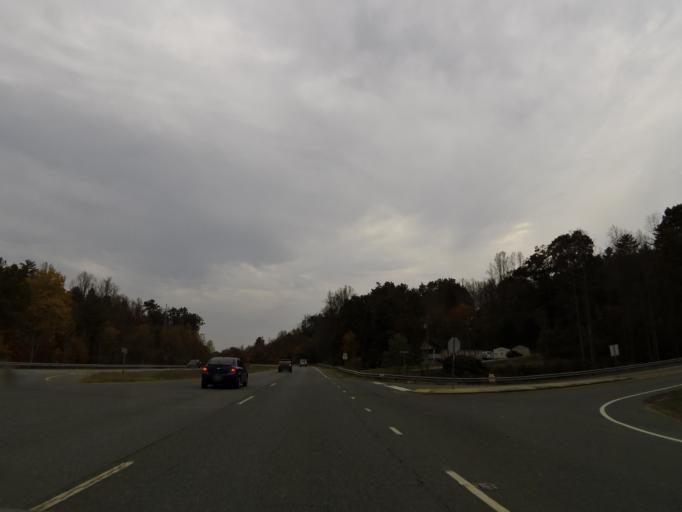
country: US
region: North Carolina
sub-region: Caldwell County
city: Lenoir
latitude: 35.9937
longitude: -81.5719
